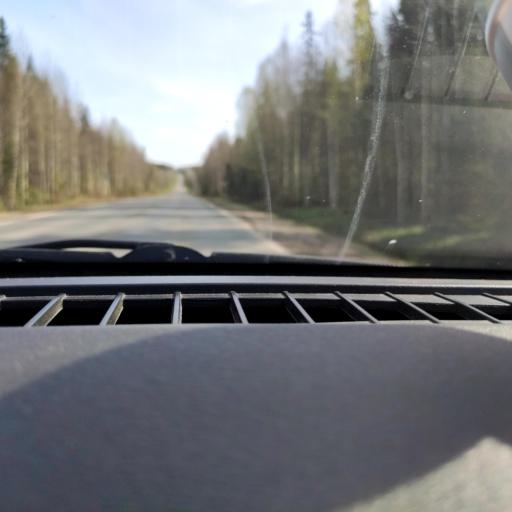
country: RU
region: Perm
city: Perm
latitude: 58.2384
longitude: 56.1591
